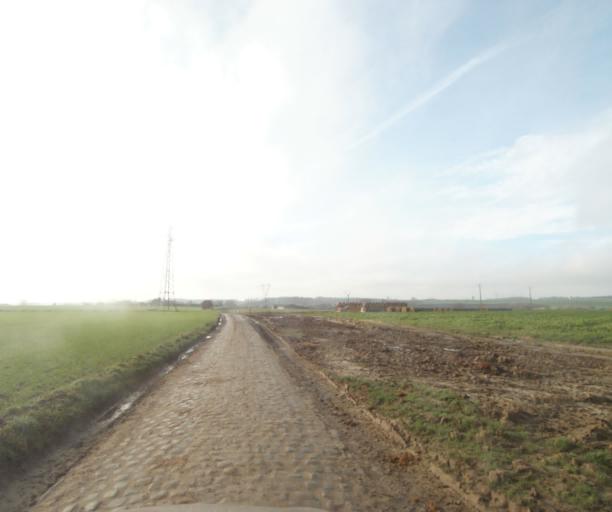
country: FR
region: Nord-Pas-de-Calais
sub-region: Departement du Nord
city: Thiant
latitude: 50.2957
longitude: 3.4627
